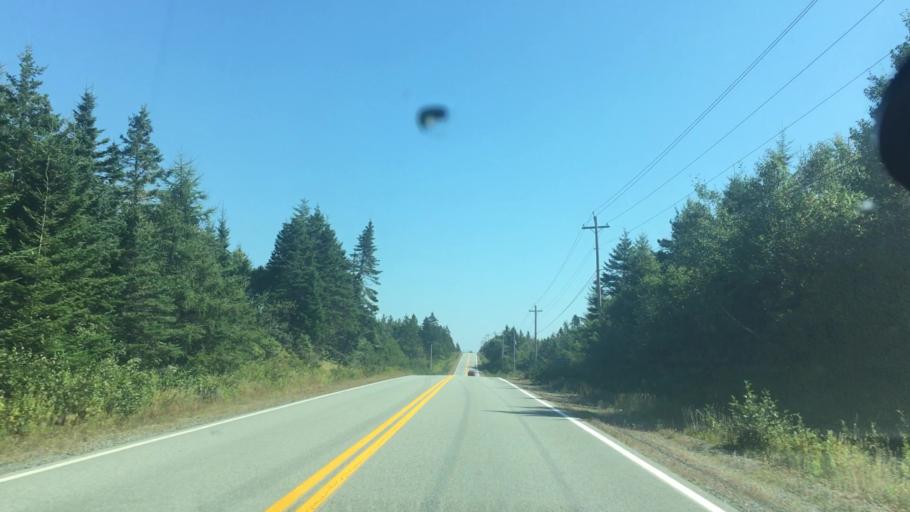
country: CA
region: Nova Scotia
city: New Glasgow
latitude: 44.9317
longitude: -62.2915
